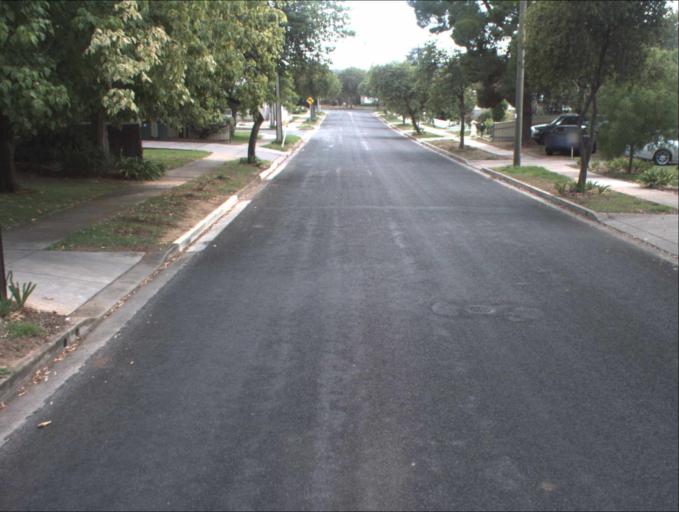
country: AU
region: South Australia
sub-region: Port Adelaide Enfield
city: Klemzig
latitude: -34.8826
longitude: 138.6305
